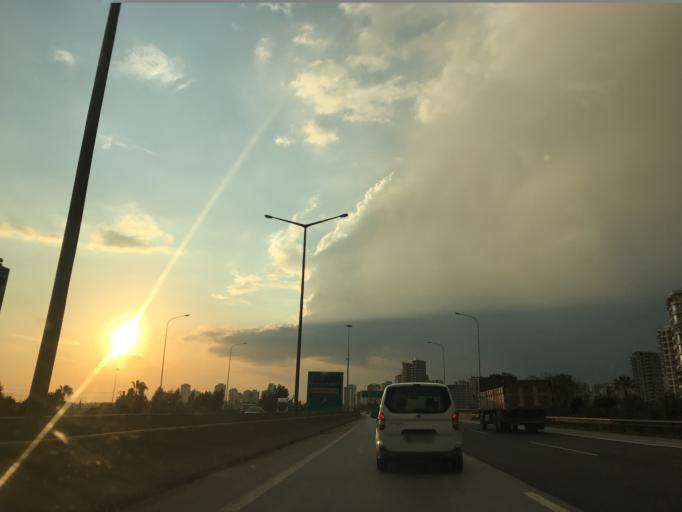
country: TR
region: Adana
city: Seyhan
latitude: 37.0324
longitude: 35.2572
